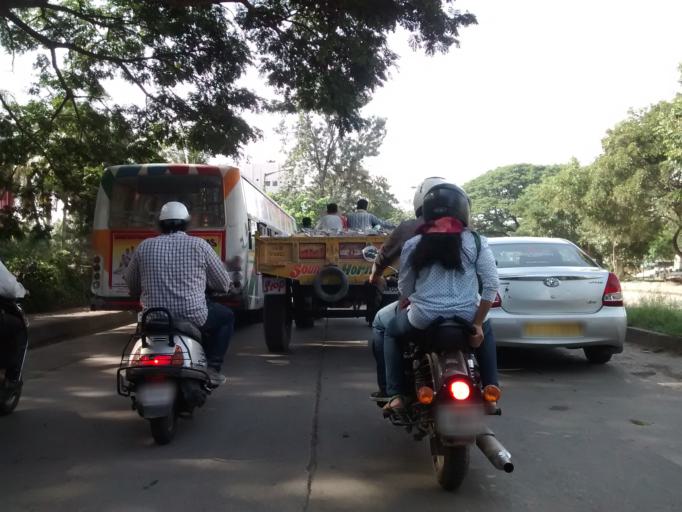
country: IN
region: Karnataka
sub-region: Bangalore Urban
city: Bangalore
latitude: 12.9855
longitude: 77.6482
